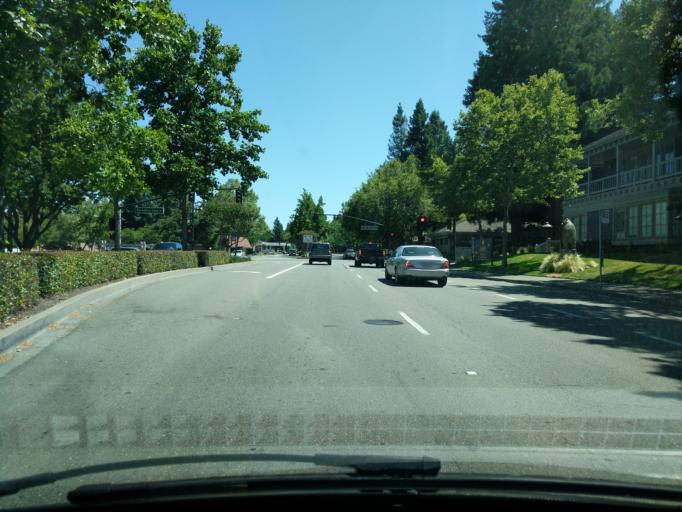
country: US
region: California
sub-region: Contra Costa County
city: Danville
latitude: 37.8136
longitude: -121.9960
